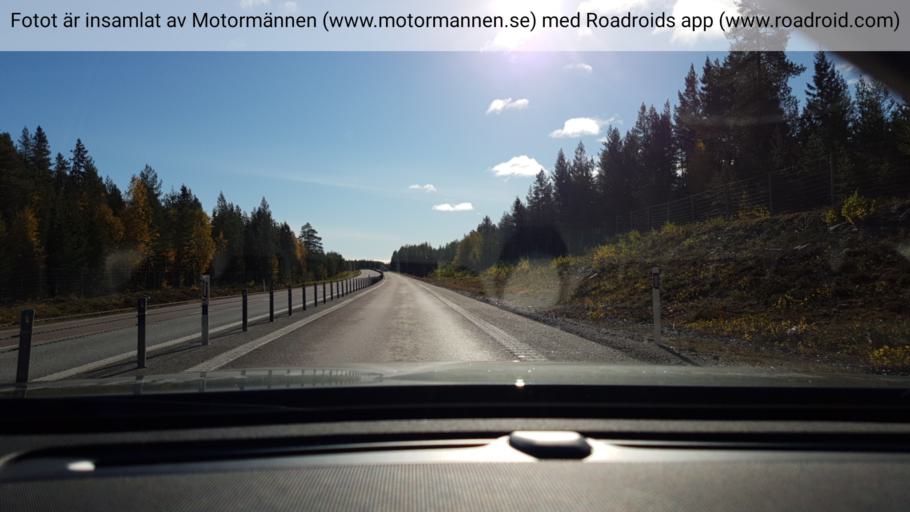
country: SE
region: Vaesterbotten
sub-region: Skelleftea Kommun
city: Soedra Bergsbyn
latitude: 64.6764
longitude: 21.0793
